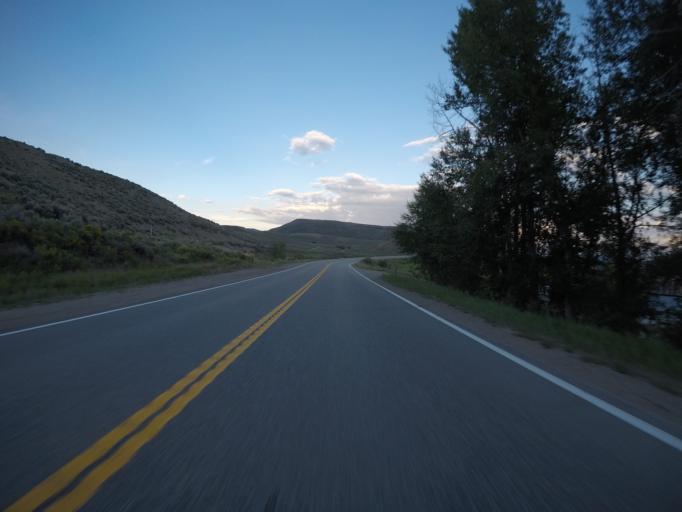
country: US
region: Colorado
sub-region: Grand County
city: Kremmling
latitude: 40.2447
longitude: -106.4453
